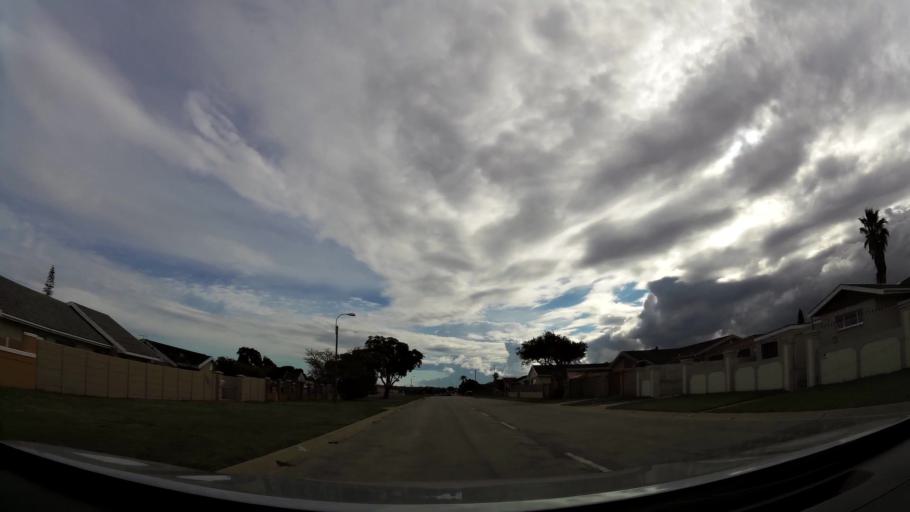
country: ZA
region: Eastern Cape
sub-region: Nelson Mandela Bay Metropolitan Municipality
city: Port Elizabeth
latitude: -33.9421
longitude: 25.4810
